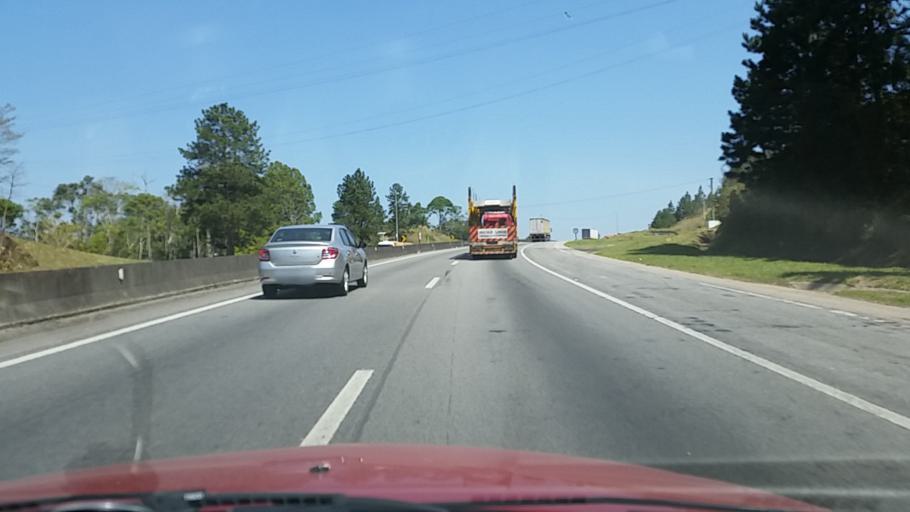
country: BR
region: Sao Paulo
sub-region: Juquitiba
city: Juquitiba
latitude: -23.9498
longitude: -47.1011
